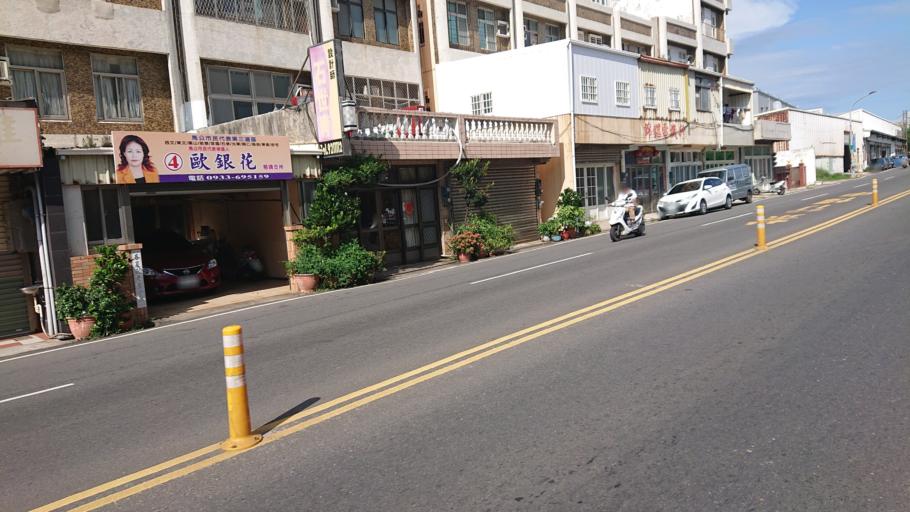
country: TW
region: Taiwan
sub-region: Penghu
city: Ma-kung
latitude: 23.5629
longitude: 119.5912
